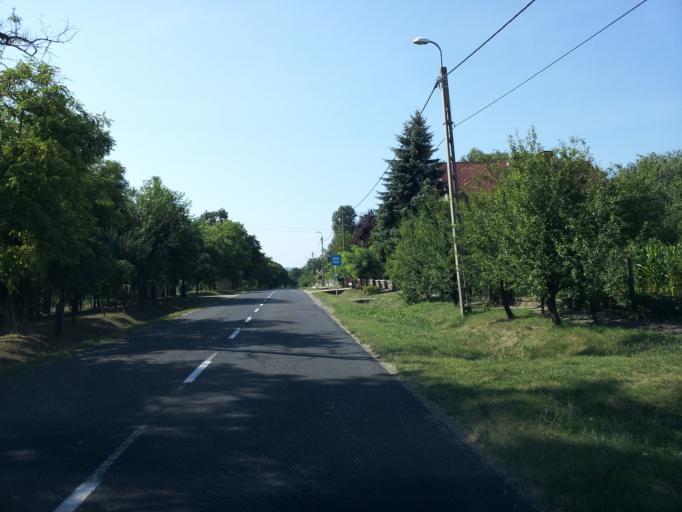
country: HU
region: Fejer
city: Lovasbereny
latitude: 47.3601
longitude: 18.5808
